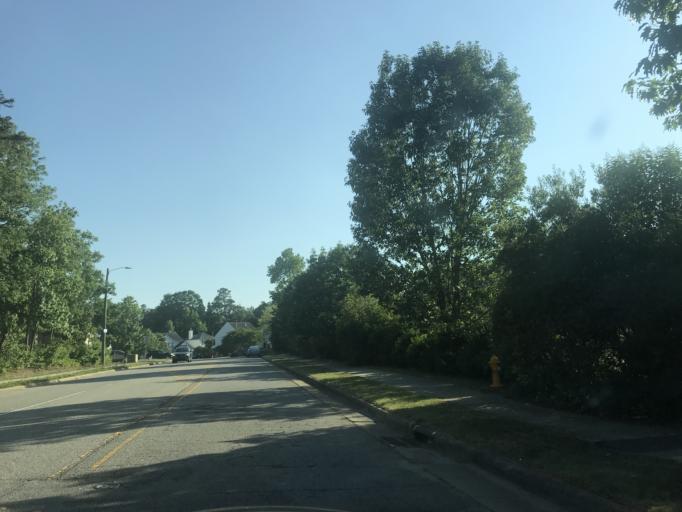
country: US
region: North Carolina
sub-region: Wake County
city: Garner
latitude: 35.7362
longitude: -78.6169
